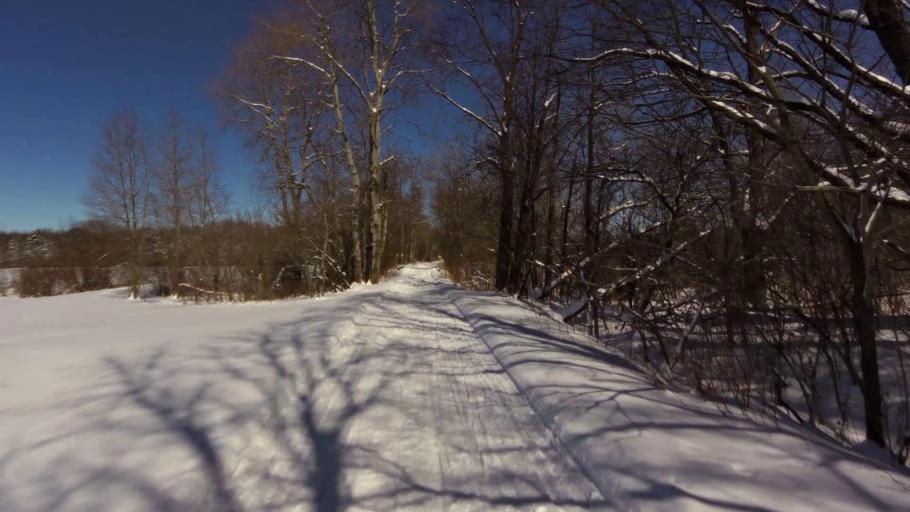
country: US
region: New York
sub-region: Chautauqua County
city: Celoron
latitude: 42.2371
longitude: -79.2694
